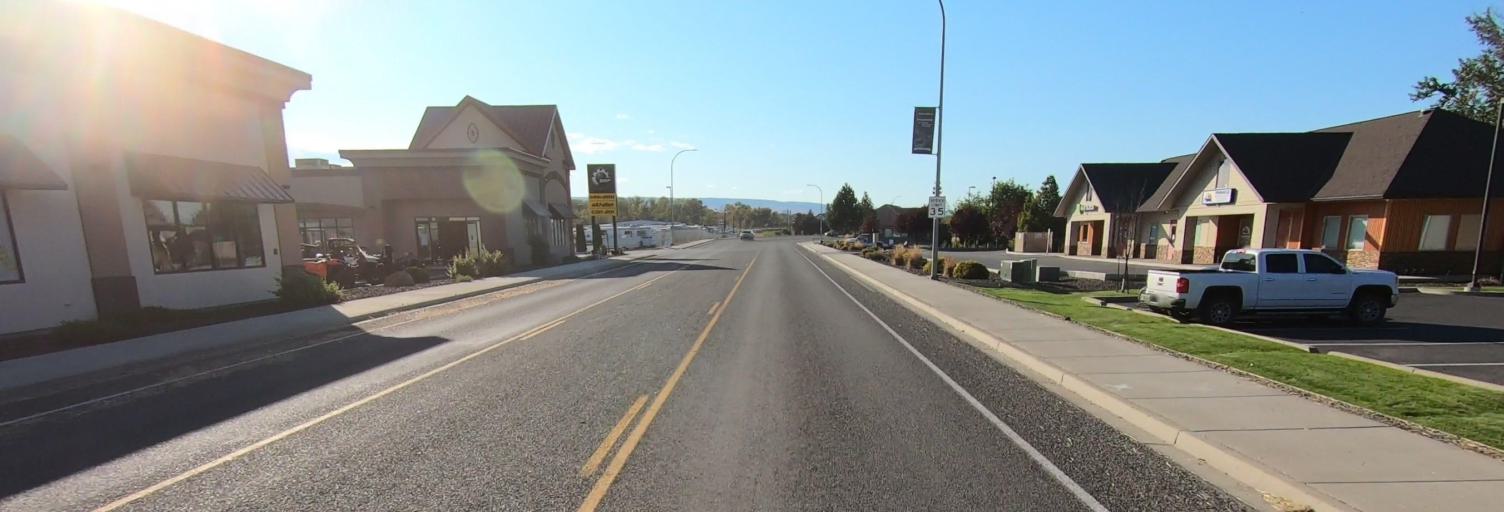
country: US
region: Washington
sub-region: Kittitas County
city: Ellensburg
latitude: 47.0034
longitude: -120.5833
